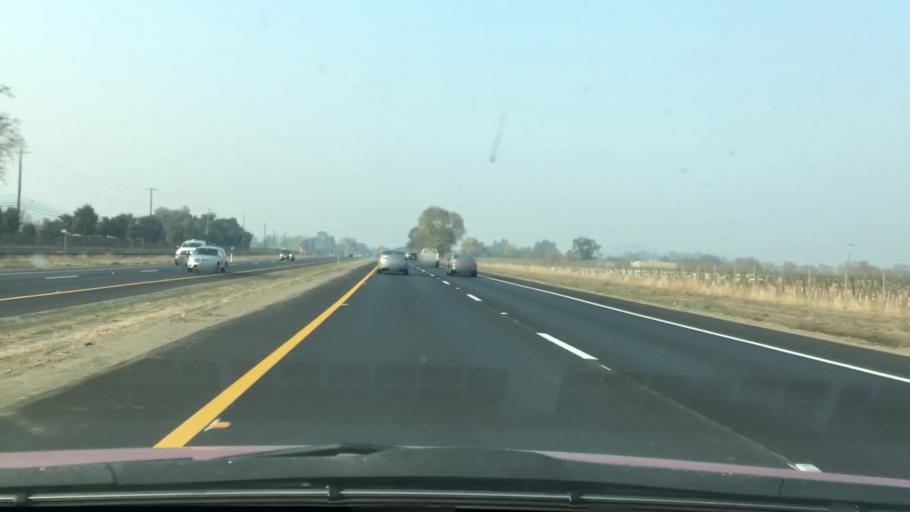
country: US
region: California
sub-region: Napa County
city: Yountville
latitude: 38.3485
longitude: -122.3290
